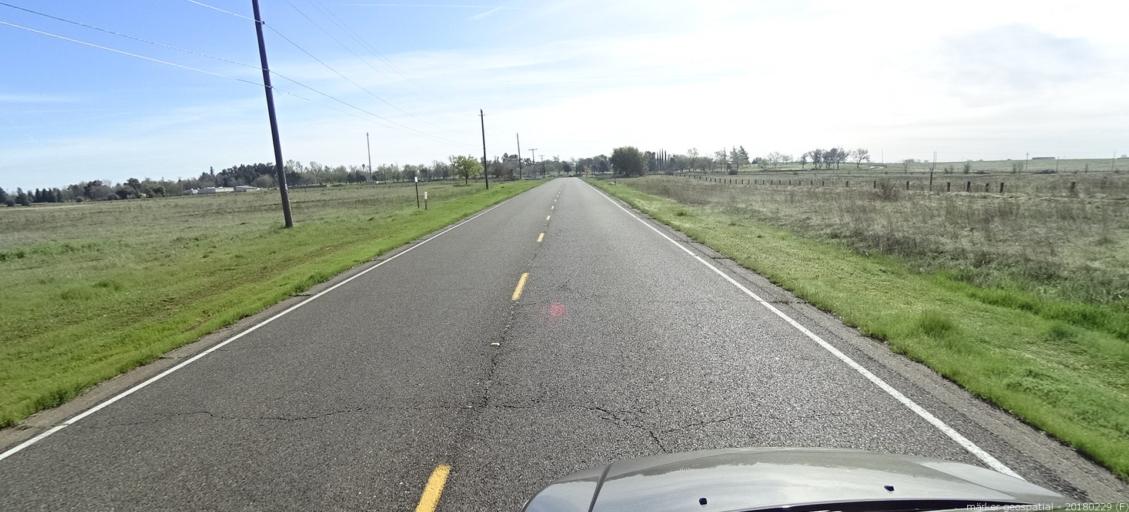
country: US
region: California
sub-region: Sacramento County
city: Rancho Cordova
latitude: 38.5466
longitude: -121.2645
